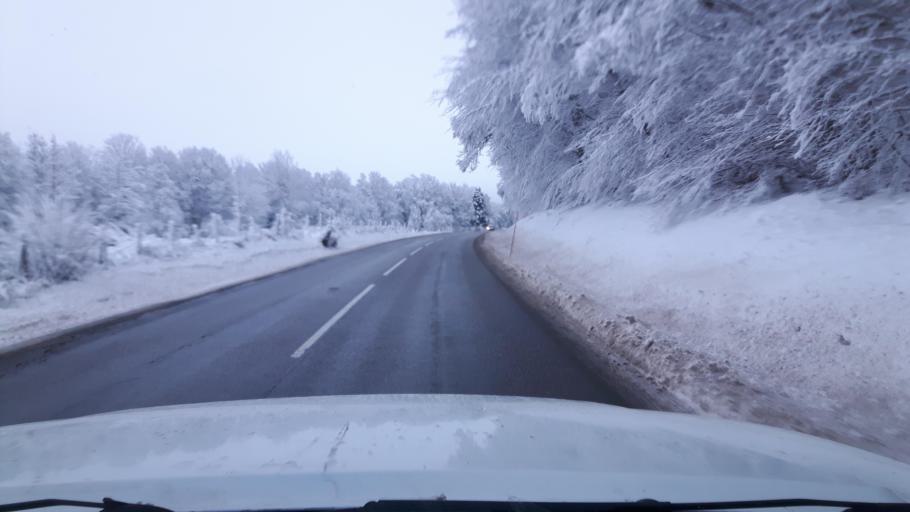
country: SE
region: Halland
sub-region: Kungsbacka Kommun
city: Fjaeras kyrkby
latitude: 57.4353
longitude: 12.1796
